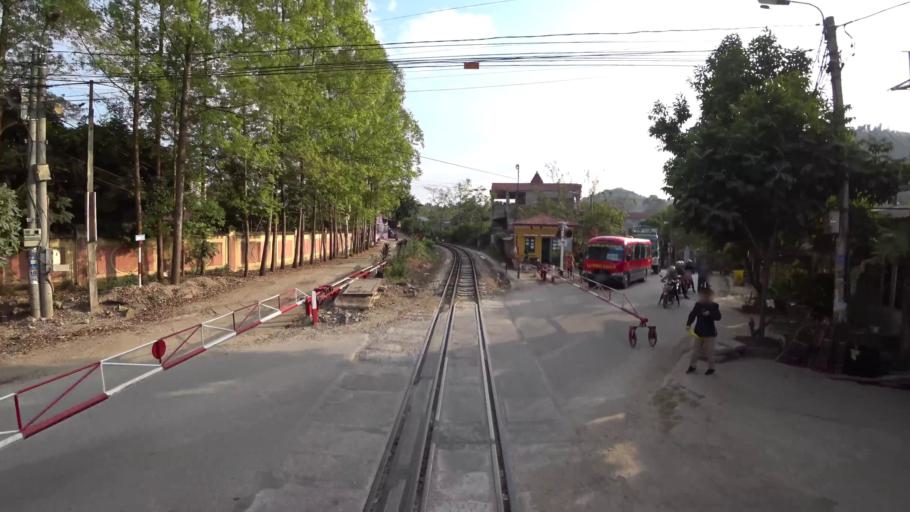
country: VN
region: Lang Son
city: Thi Tran Cao Loc
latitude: 21.9361
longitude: 106.6970
